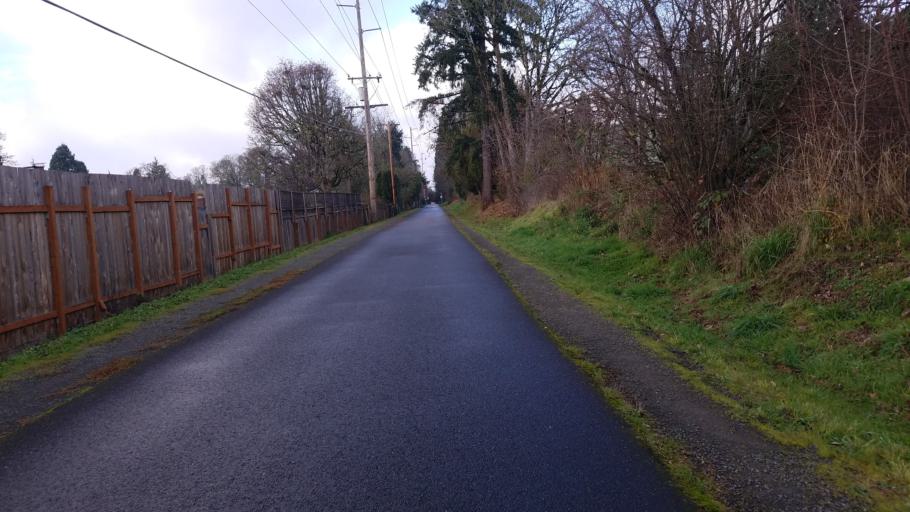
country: US
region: Oregon
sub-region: Clackamas County
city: Jennings Lodge
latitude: 45.4011
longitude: -122.6274
